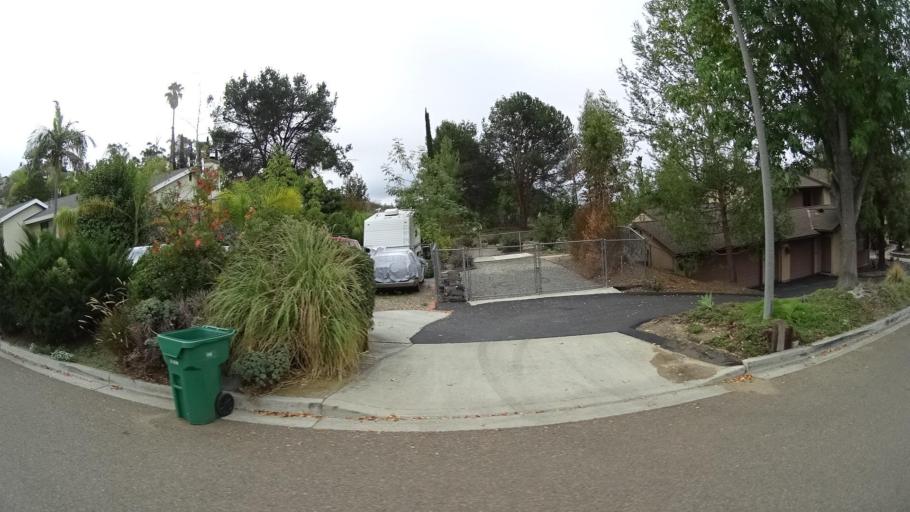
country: US
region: California
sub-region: San Diego County
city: Rancho San Diego
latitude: 32.7703
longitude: -116.9218
